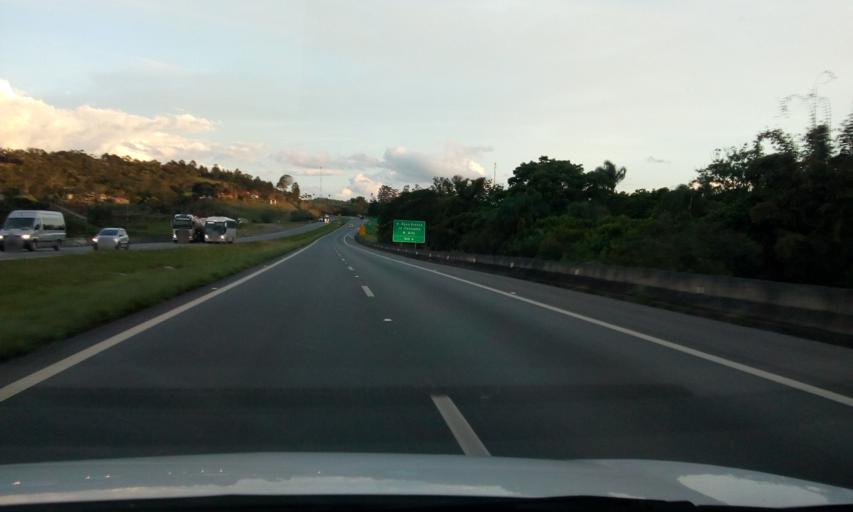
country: BR
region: Sao Paulo
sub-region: Santa Isabel
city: Santa Isabel
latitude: -23.1828
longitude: -46.2044
